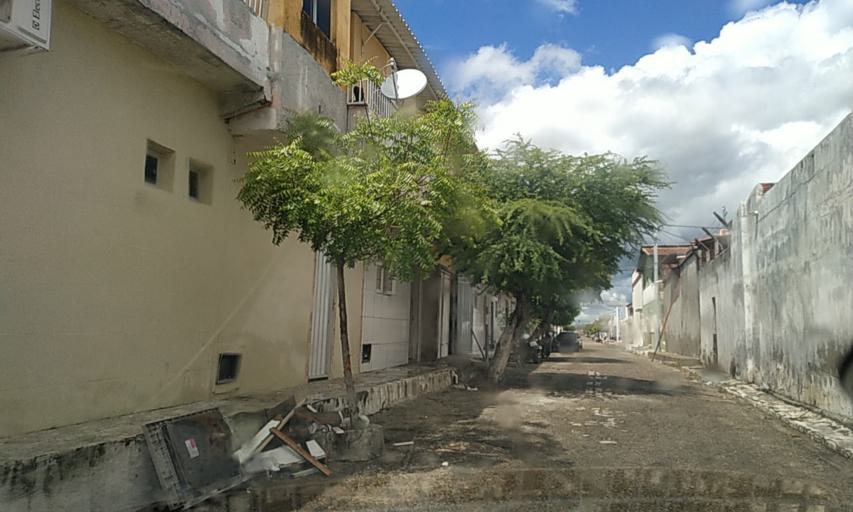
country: BR
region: Rio Grande do Norte
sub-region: Areia Branca
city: Areia Branca
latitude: -4.9517
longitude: -37.1337
